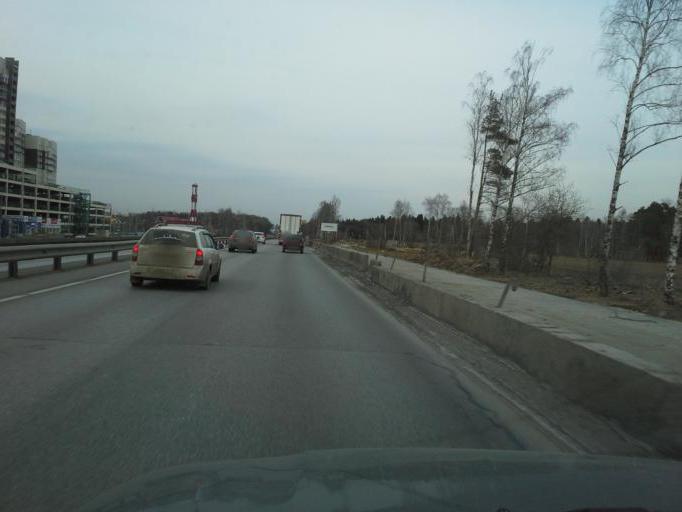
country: RU
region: Moskovskaya
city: Odintsovo
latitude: 55.6606
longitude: 37.3017
